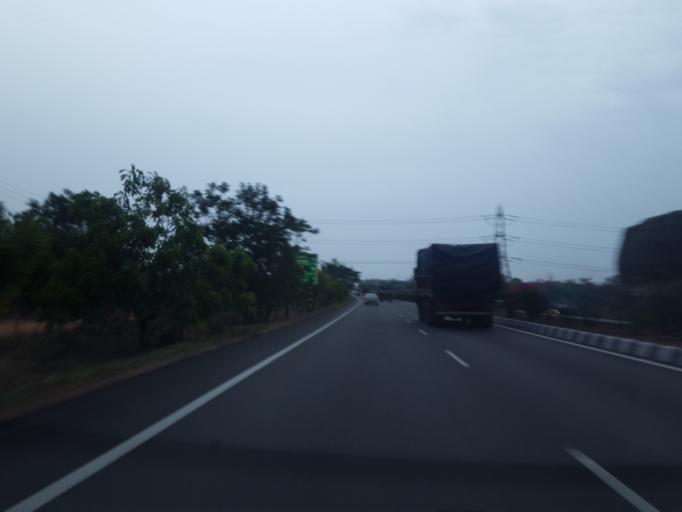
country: IN
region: Telangana
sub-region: Mahbubnagar
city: Farrukhnagar
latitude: 17.0854
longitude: 78.2346
